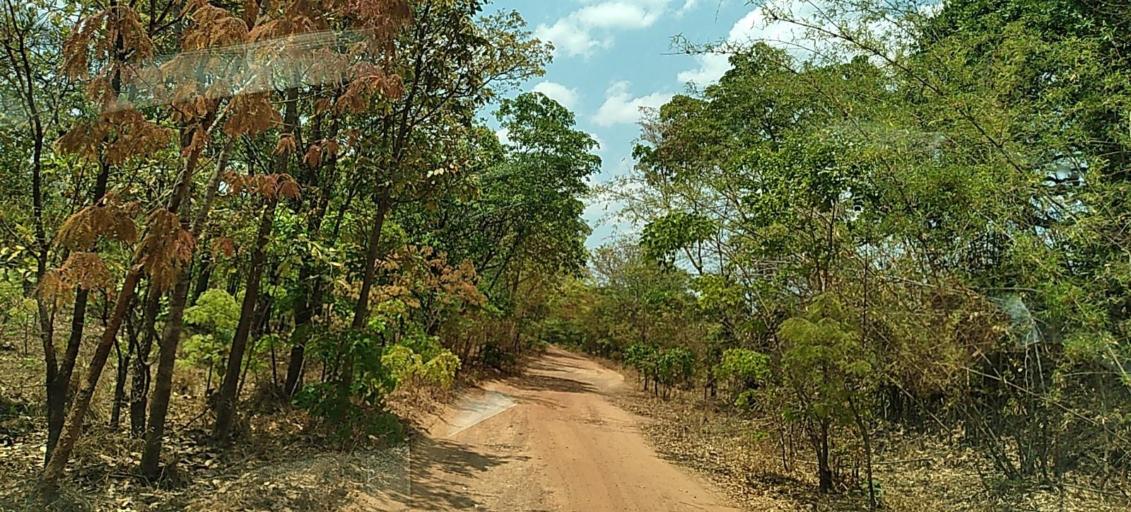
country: ZM
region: Copperbelt
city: Chililabombwe
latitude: -12.5120
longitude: 27.6296
